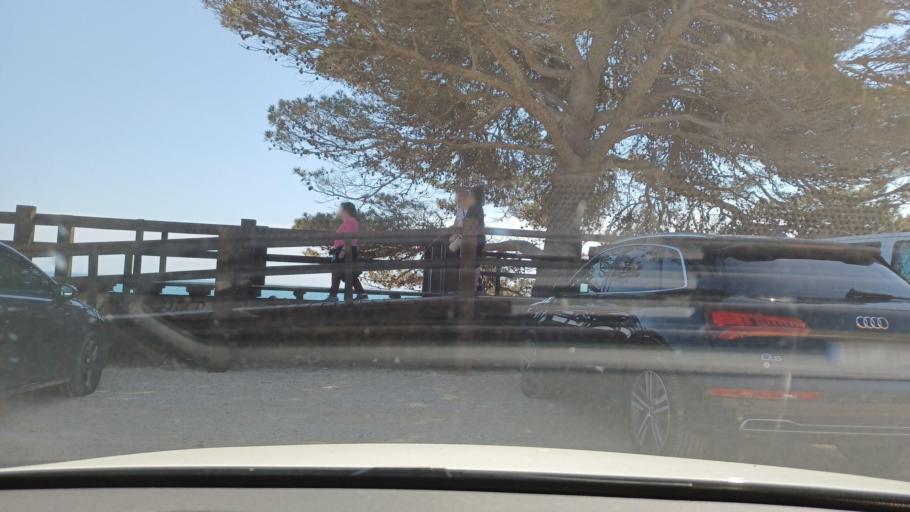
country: ES
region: Catalonia
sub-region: Provincia de Tarragona
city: L'Ampolla
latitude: 40.8308
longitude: 0.7414
